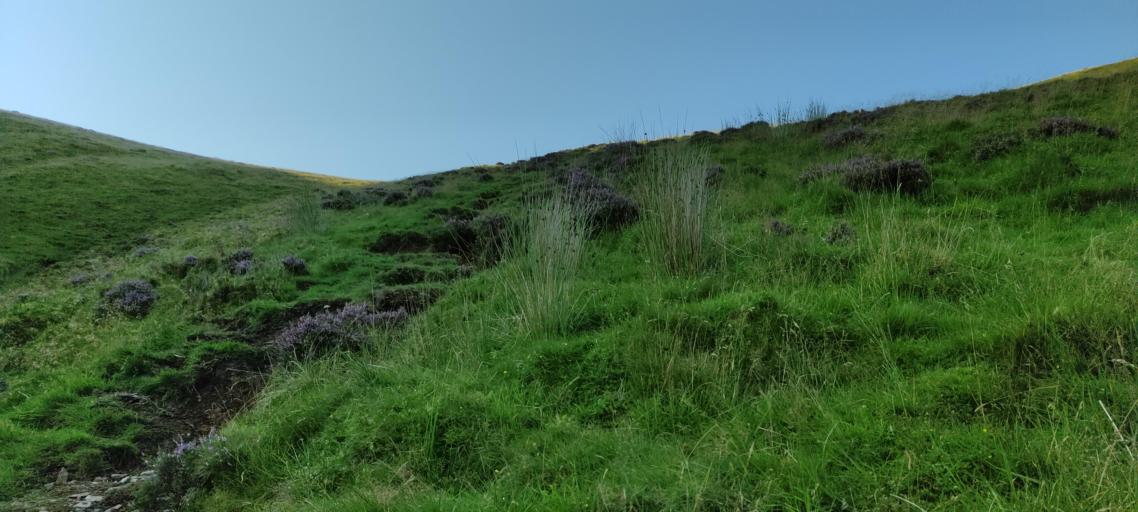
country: GB
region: England
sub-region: Cumbria
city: Cockermouth
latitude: 54.5696
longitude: -3.3817
